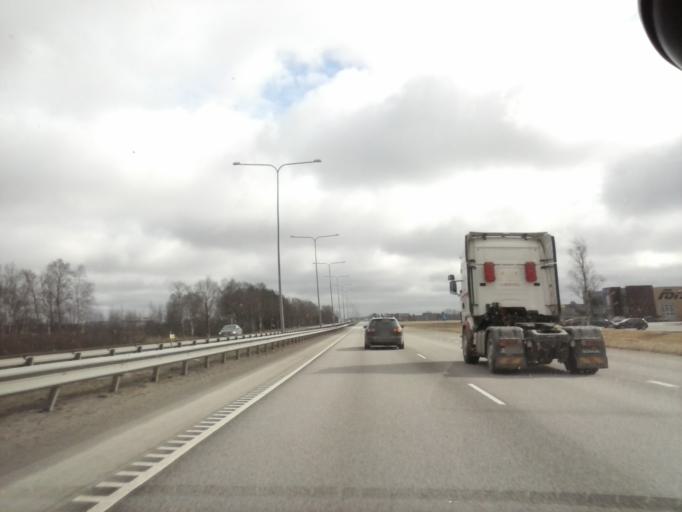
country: EE
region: Harju
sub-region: Rae vald
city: Jueri
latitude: 59.3929
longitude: 24.8245
